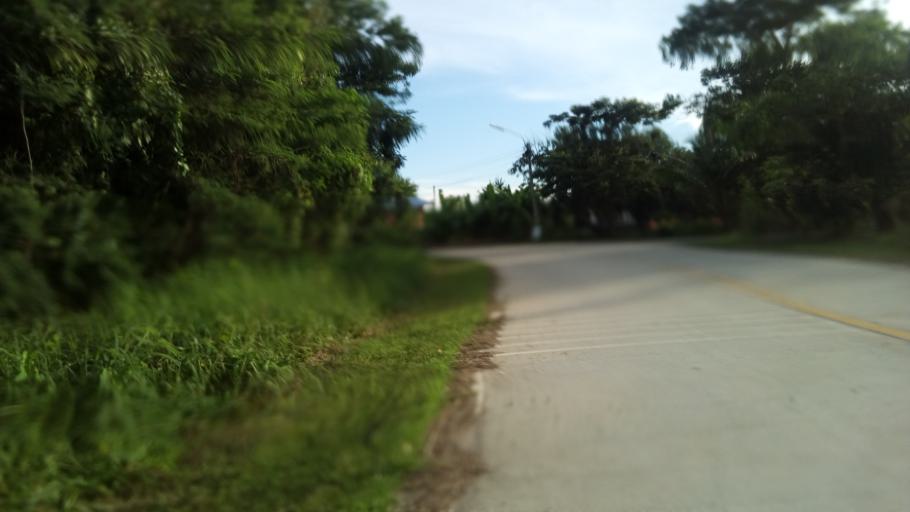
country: TH
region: Pathum Thani
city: Ban Lam Luk Ka
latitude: 14.0086
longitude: 100.8453
